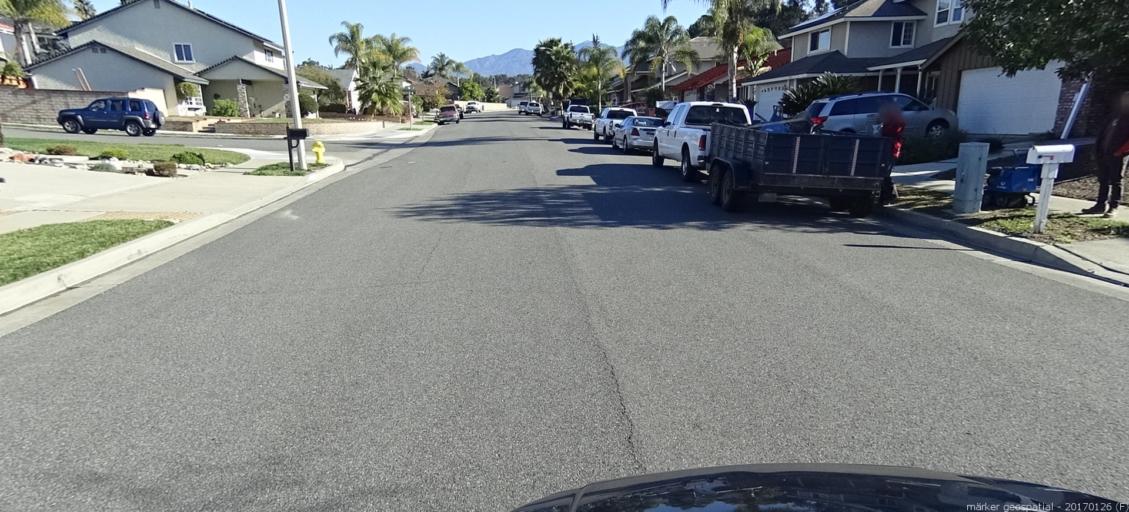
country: US
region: California
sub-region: Orange County
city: Lake Forest
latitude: 33.6321
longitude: -117.6832
